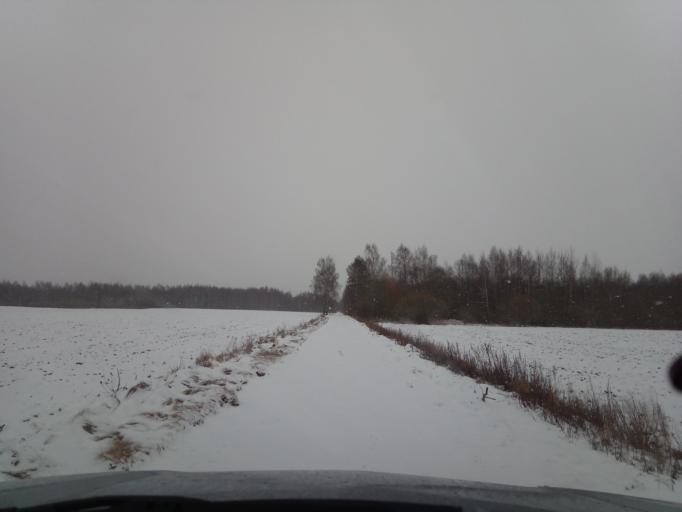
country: LT
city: Ramygala
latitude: 55.5870
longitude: 24.3704
